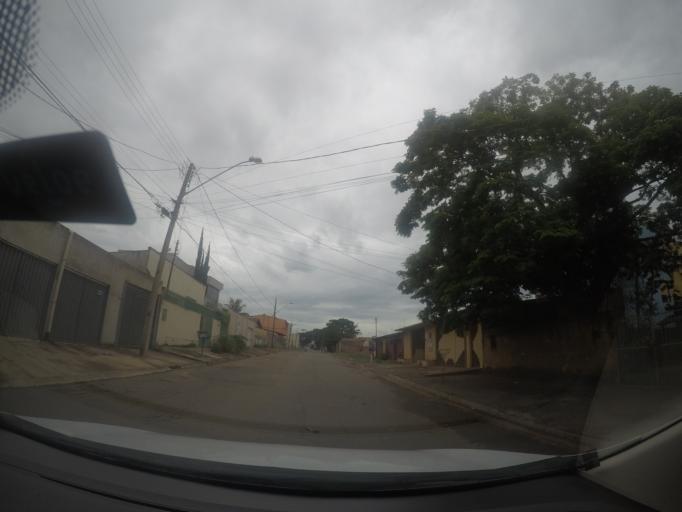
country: BR
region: Goias
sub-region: Goiania
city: Goiania
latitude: -16.6616
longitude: -49.3108
